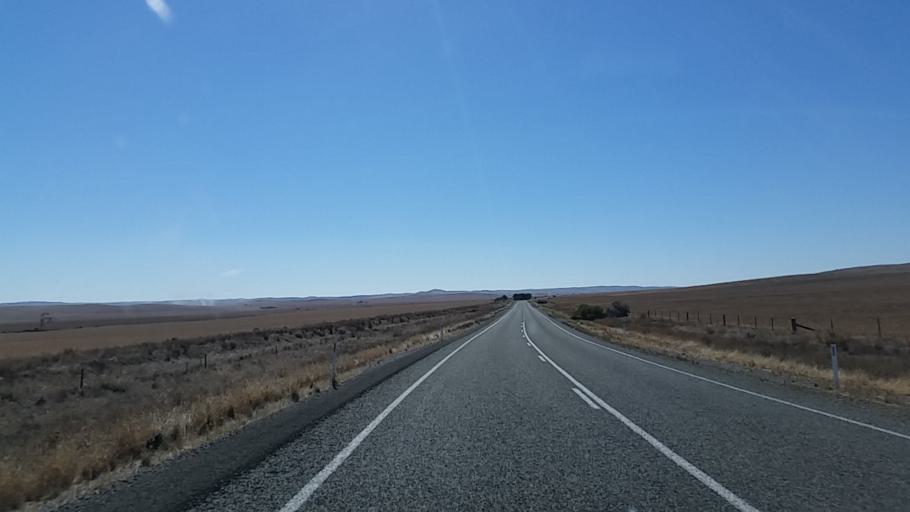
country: AU
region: South Australia
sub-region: Northern Areas
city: Jamestown
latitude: -33.3060
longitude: 138.8775
